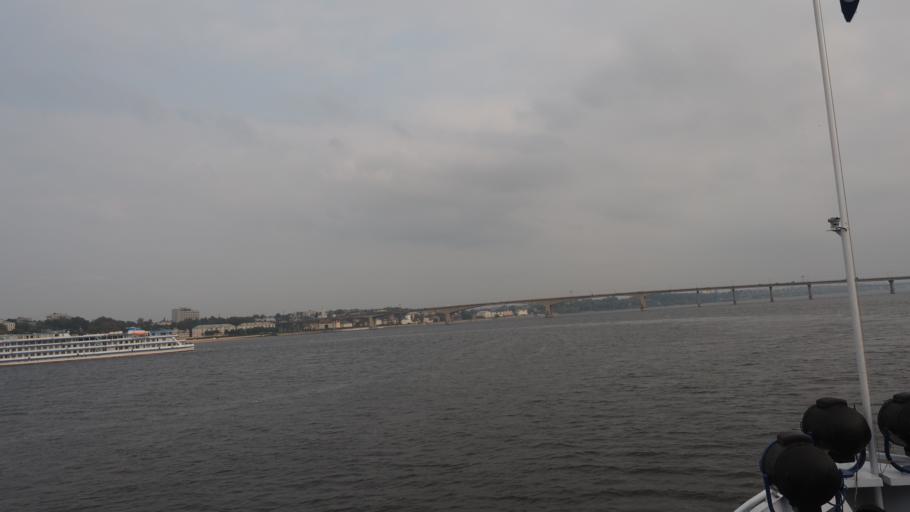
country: RU
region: Kostroma
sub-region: Kostromskoy Rayon
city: Kostroma
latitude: 57.7560
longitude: 40.9247
